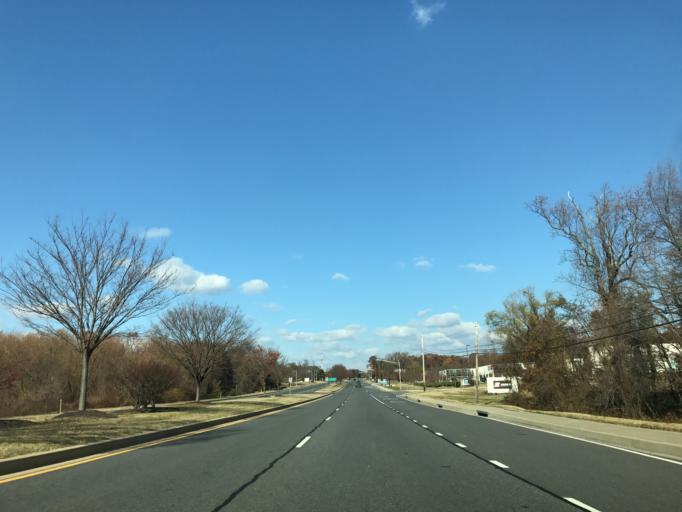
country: US
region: Maryland
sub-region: Anne Arundel County
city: Ferndale
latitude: 39.1760
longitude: -76.6488
